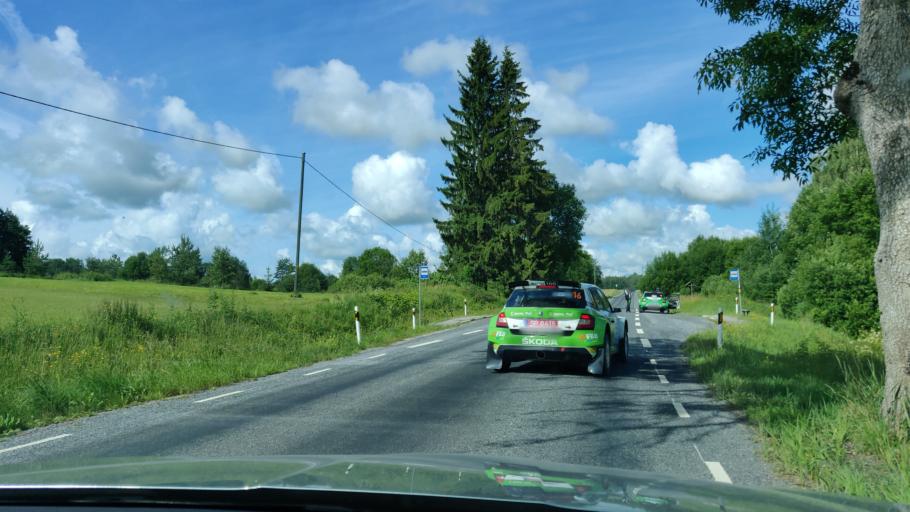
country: EE
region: Tartu
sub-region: Elva linn
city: Elva
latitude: 58.0381
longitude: 26.3624
